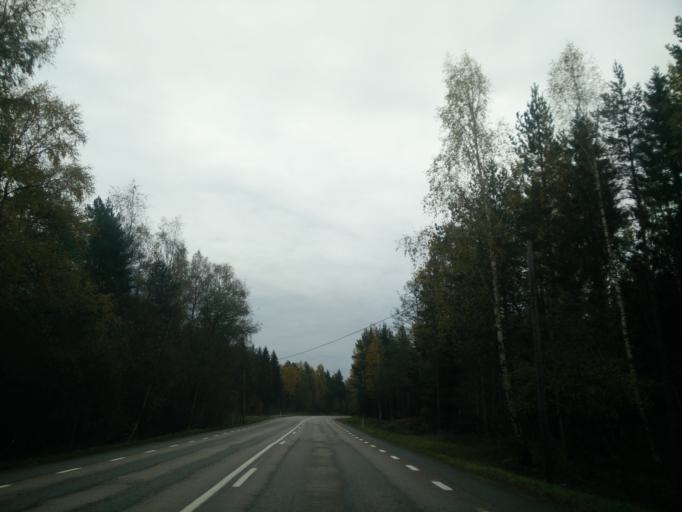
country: SE
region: Gaevleborg
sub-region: Gavle Kommun
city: Norrsundet
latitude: 60.8823
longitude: 17.1407
